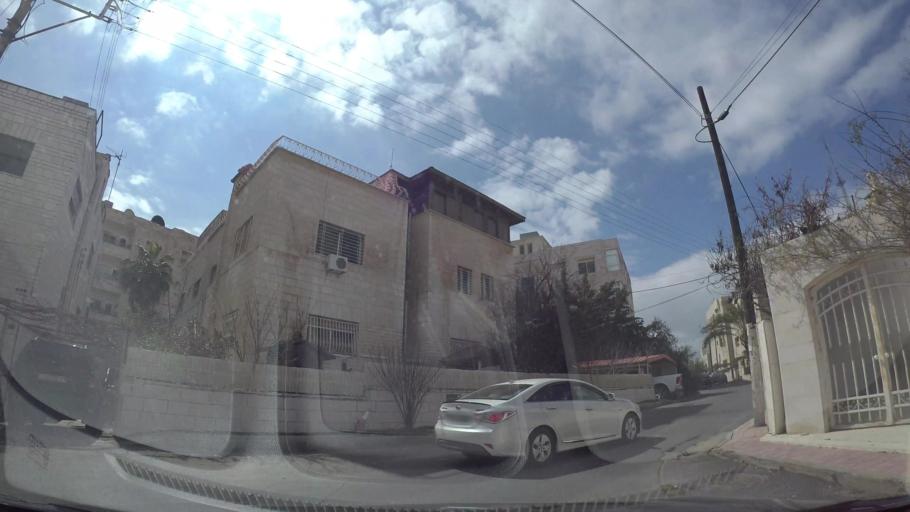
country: JO
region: Amman
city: Wadi as Sir
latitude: 31.9694
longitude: 35.8382
